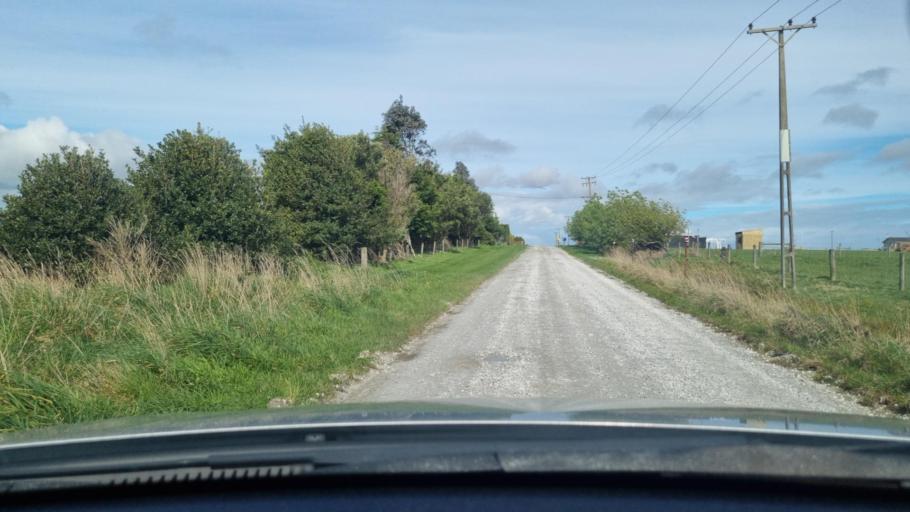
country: NZ
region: Southland
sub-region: Invercargill City
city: Invercargill
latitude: -46.4524
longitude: 168.3822
